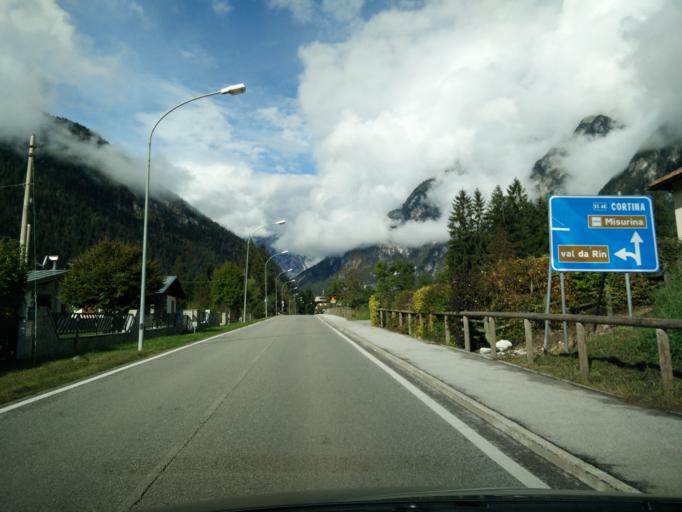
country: IT
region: Veneto
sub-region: Provincia di Belluno
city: Auronzo
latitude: 46.5672
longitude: 12.4050
